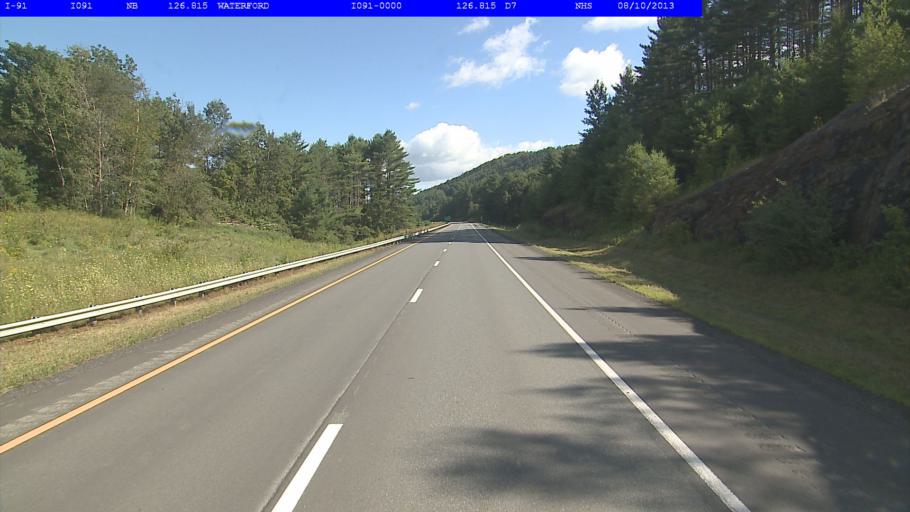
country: US
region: Vermont
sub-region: Caledonia County
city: Saint Johnsbury
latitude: 44.3760
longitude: -72.0208
